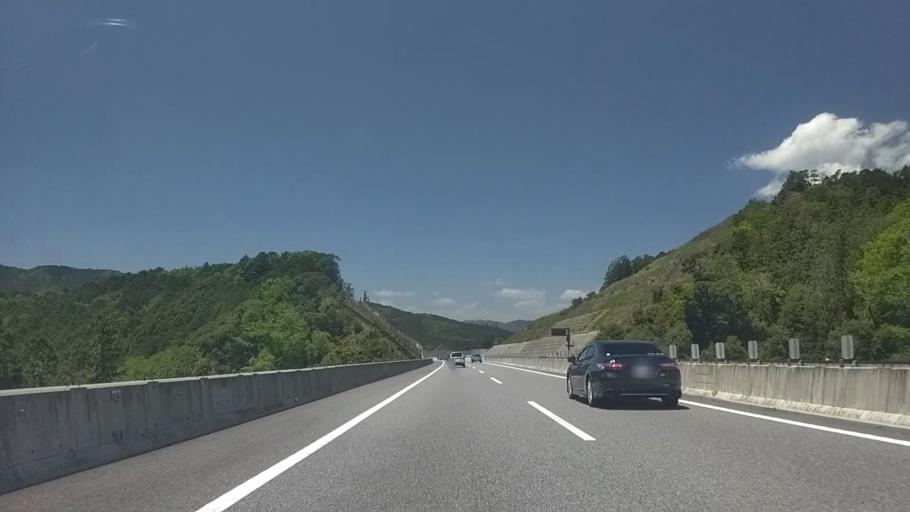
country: JP
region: Aichi
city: Shinshiro
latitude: 34.9050
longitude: 137.6149
